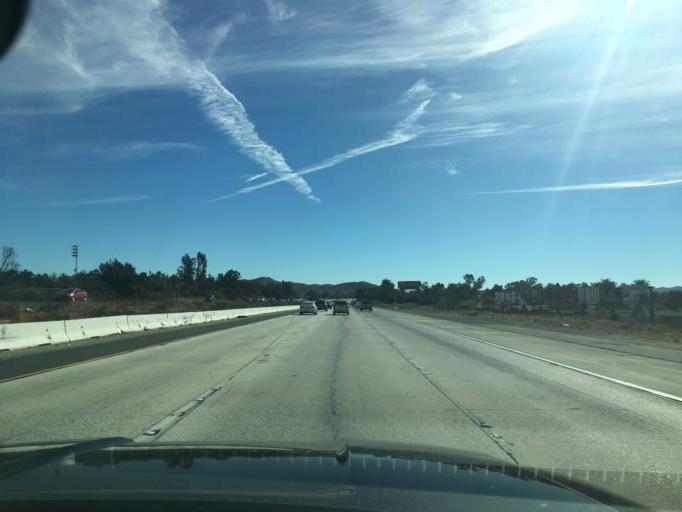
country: US
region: California
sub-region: Riverside County
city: Lake Elsinore
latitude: 33.7016
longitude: -117.3511
